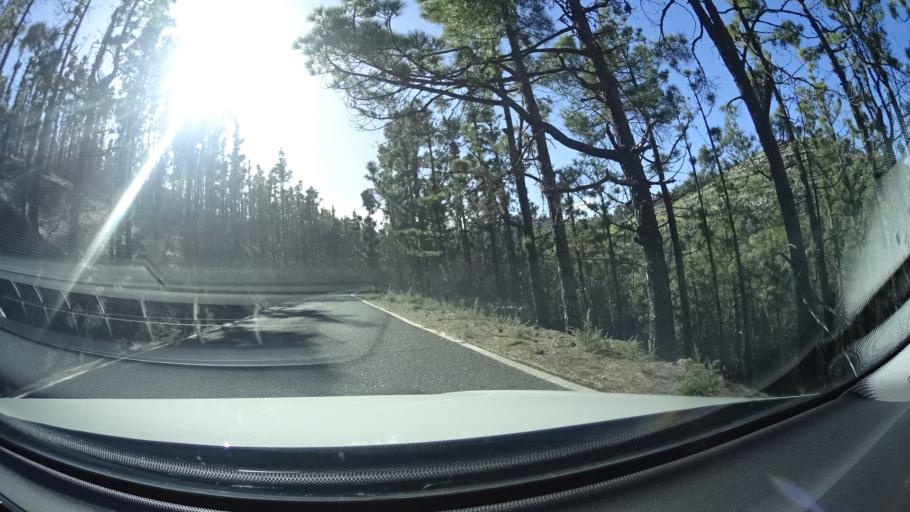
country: ES
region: Canary Islands
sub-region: Provincia de Las Palmas
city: San Bartolome
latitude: 27.9652
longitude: -15.5556
